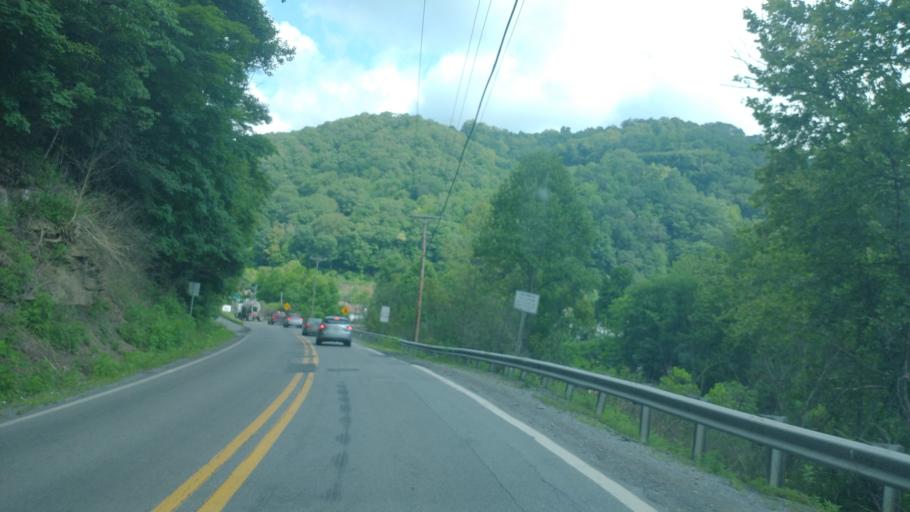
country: US
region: West Virginia
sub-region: McDowell County
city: Welch
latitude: 37.4133
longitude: -81.4265
